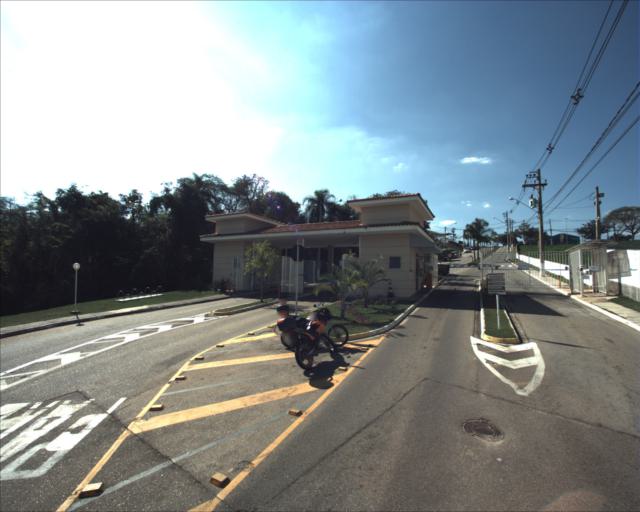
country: BR
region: Sao Paulo
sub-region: Sorocaba
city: Sorocaba
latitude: -23.4537
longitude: -47.5118
